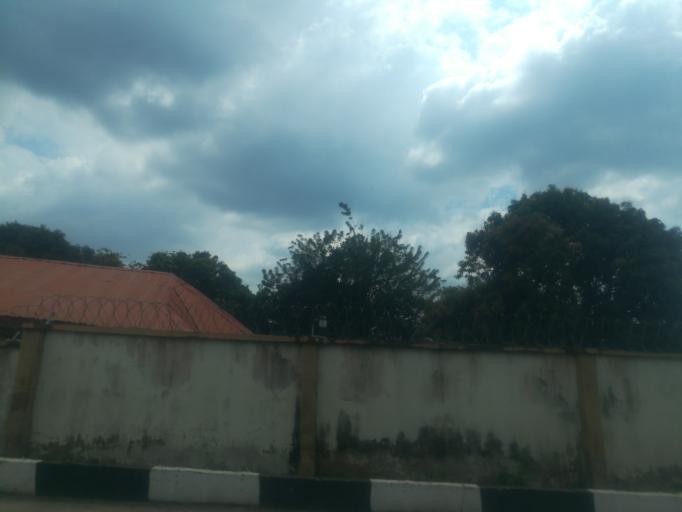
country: NG
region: Oyo
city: Ibadan
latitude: 7.3967
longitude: 3.8777
